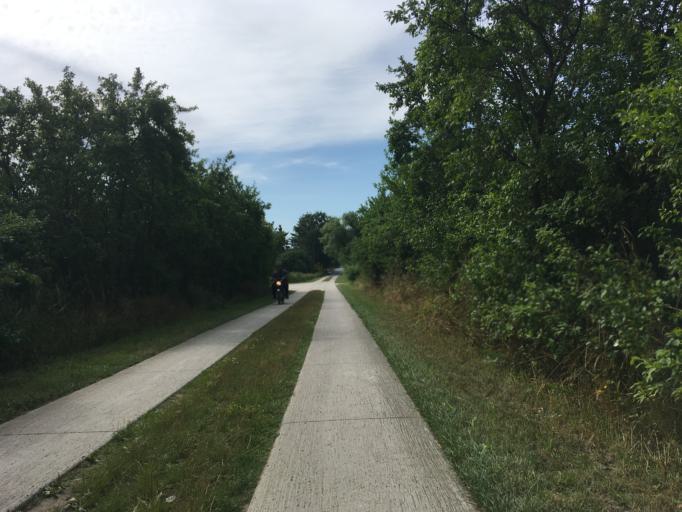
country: DE
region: Brandenburg
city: Zichow
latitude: 53.2157
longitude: 14.0441
